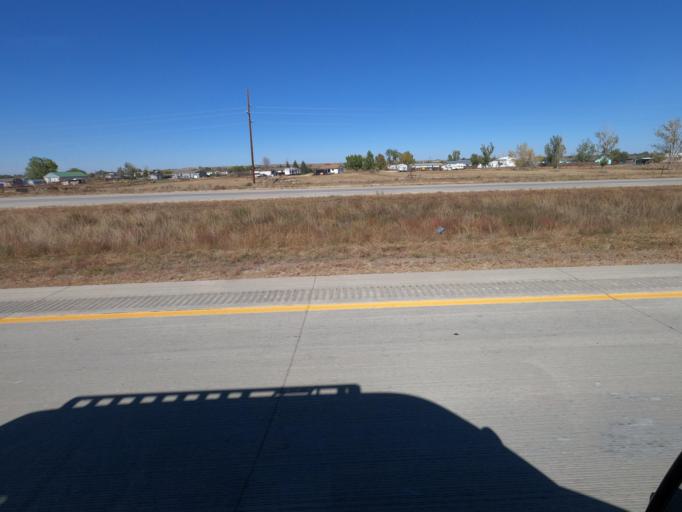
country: US
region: Colorado
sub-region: Morgan County
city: Fort Morgan
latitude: 40.2654
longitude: -103.8558
